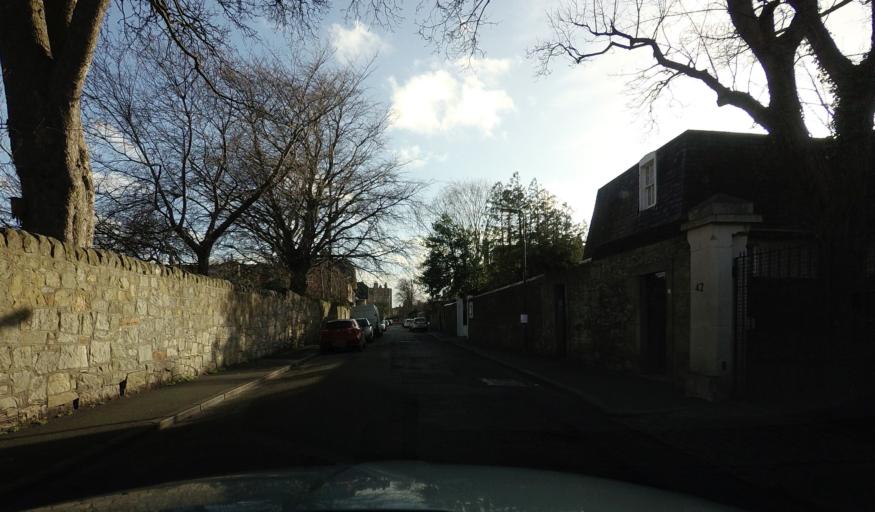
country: GB
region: Scotland
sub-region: Edinburgh
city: Edinburgh
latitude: 55.9785
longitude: -3.2013
